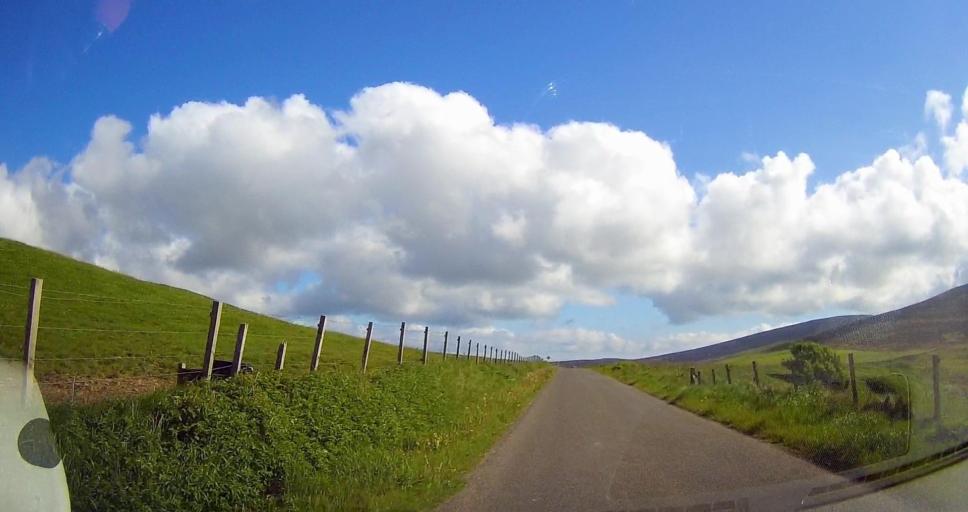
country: GB
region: Scotland
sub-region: Orkney Islands
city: Stromness
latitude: 58.9778
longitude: -3.1352
